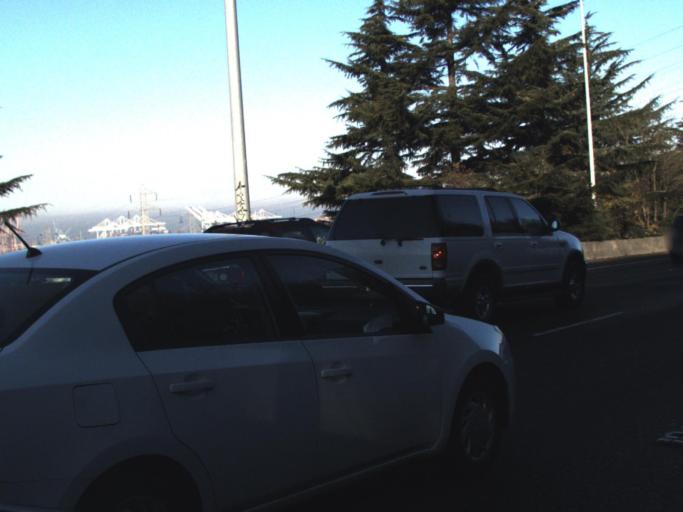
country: US
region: Washington
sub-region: King County
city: Seattle
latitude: 47.5627
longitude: -122.3213
